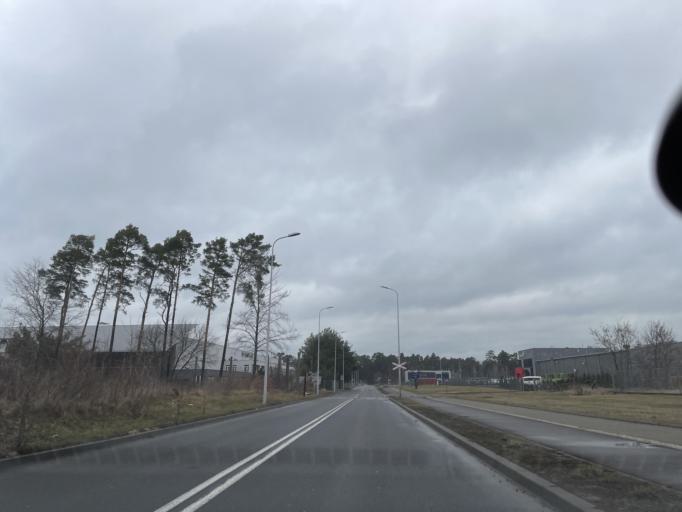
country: PL
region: Kujawsko-Pomorskie
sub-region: Bydgoszcz
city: Bydgoszcz
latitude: 53.0939
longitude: 18.0564
